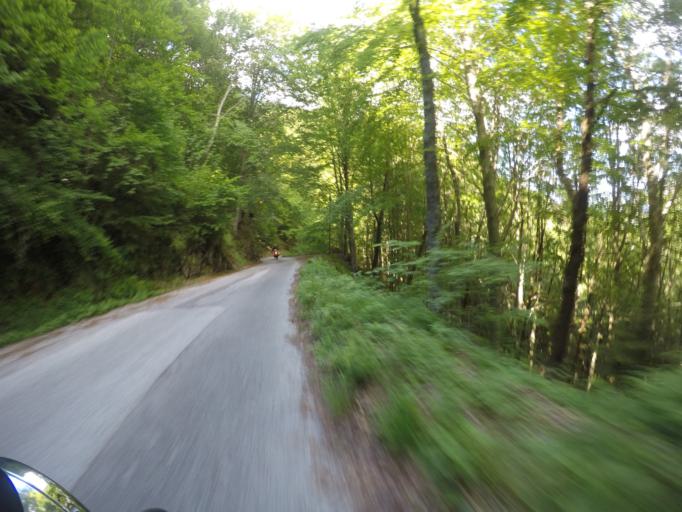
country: IT
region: Tuscany
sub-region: Provincia di Lucca
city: Minucciano
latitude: 44.1495
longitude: 10.1942
